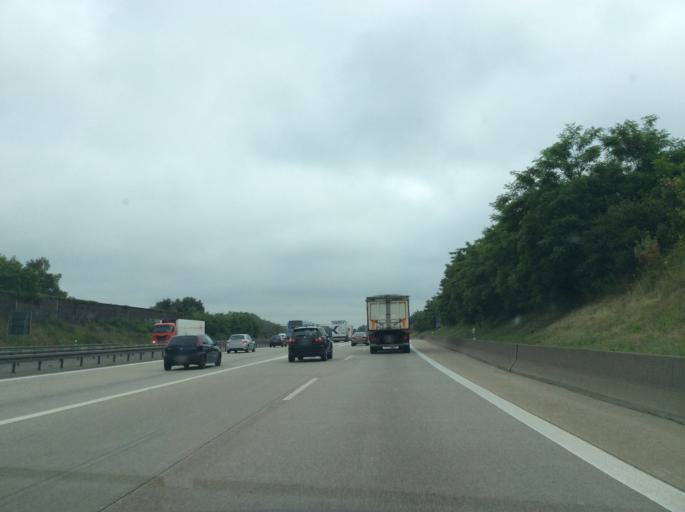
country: DE
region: Saxony
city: Albertstadt
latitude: 51.1173
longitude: 13.7450
